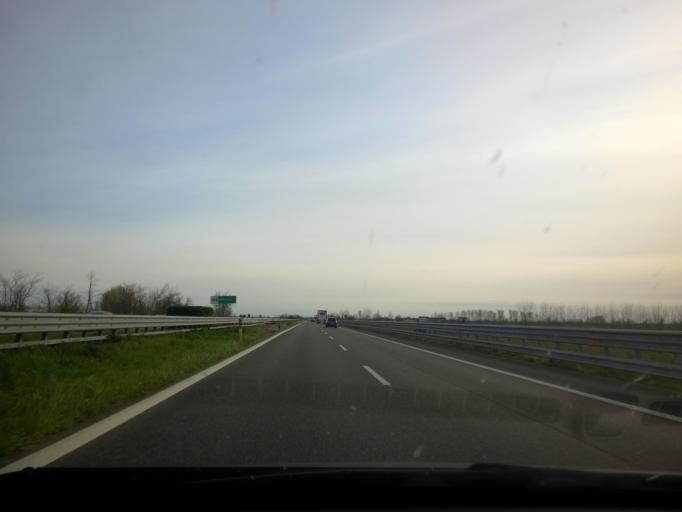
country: IT
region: Lombardy
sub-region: Provincia di Brescia
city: San Gervasio Bresciano
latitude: 45.2982
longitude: 10.1375
